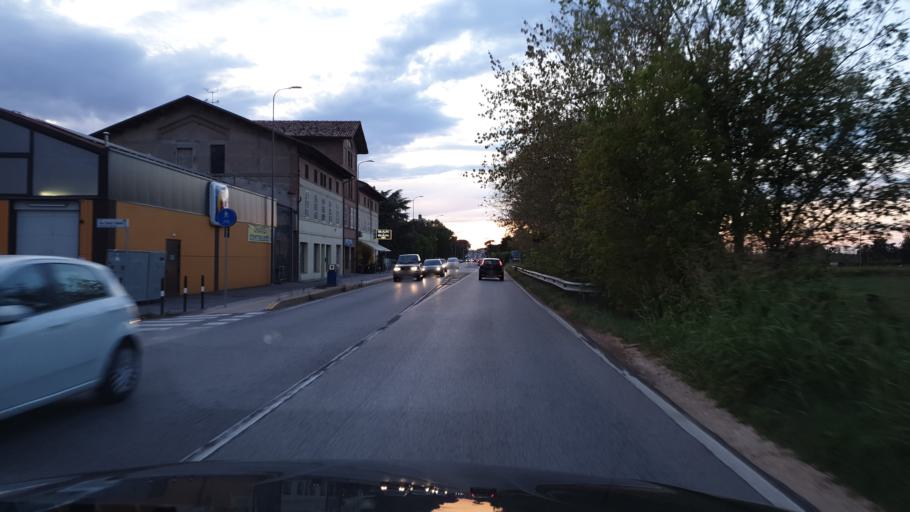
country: IT
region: Emilia-Romagna
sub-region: Provincia di Ravenna
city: Mezzano
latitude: 44.4637
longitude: 12.0922
